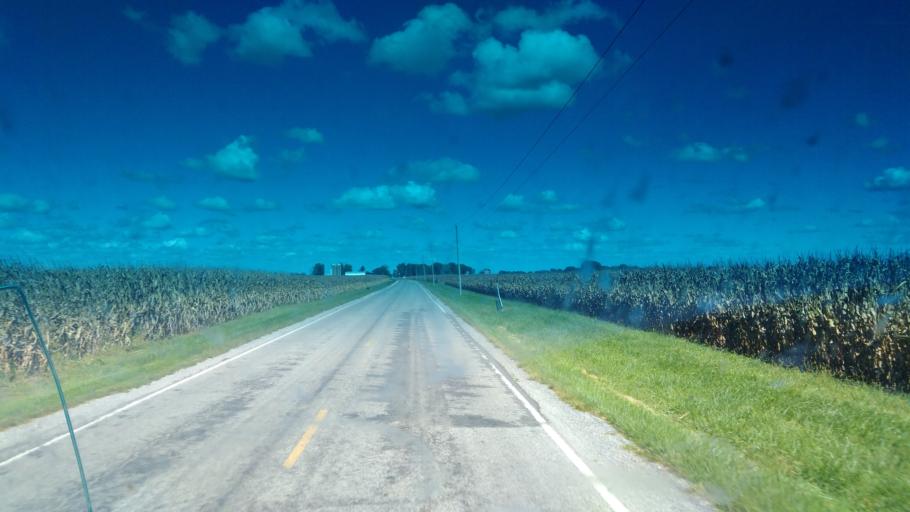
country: US
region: Ohio
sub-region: Madison County
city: Plain City
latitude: 40.0391
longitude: -83.3589
